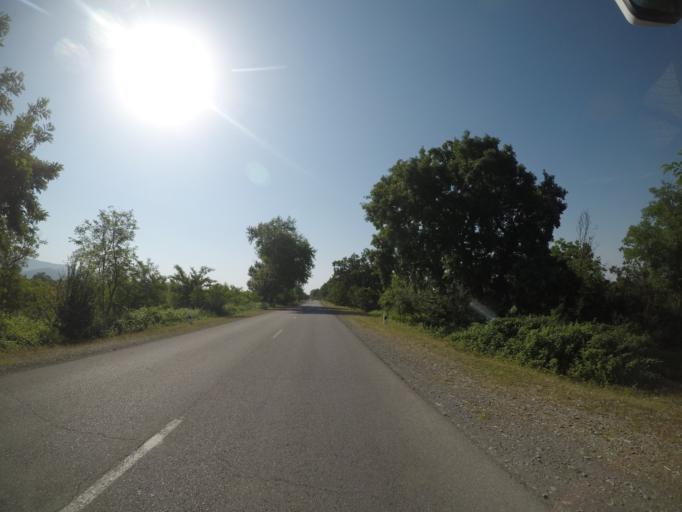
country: AZ
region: Oguz
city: Oguz
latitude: 41.0810
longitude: 47.2993
